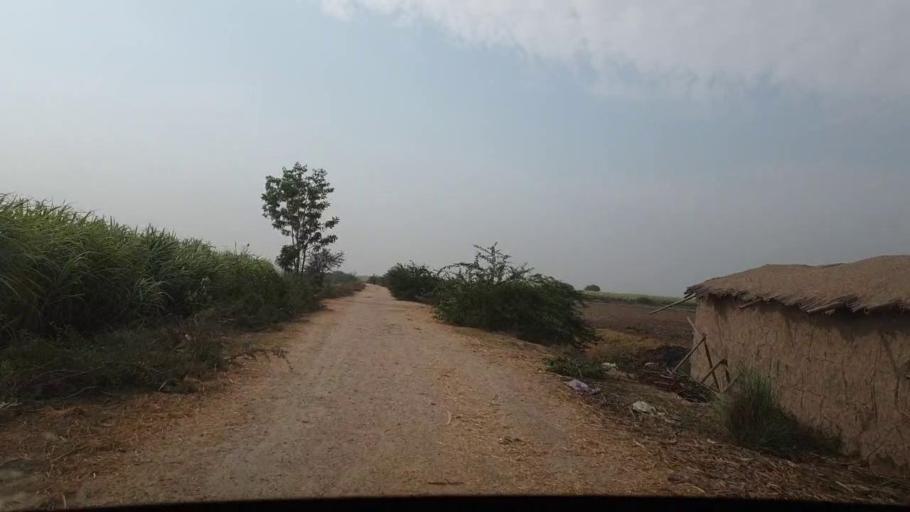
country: PK
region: Sindh
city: Chuhar Jamali
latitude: 24.4147
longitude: 67.9392
